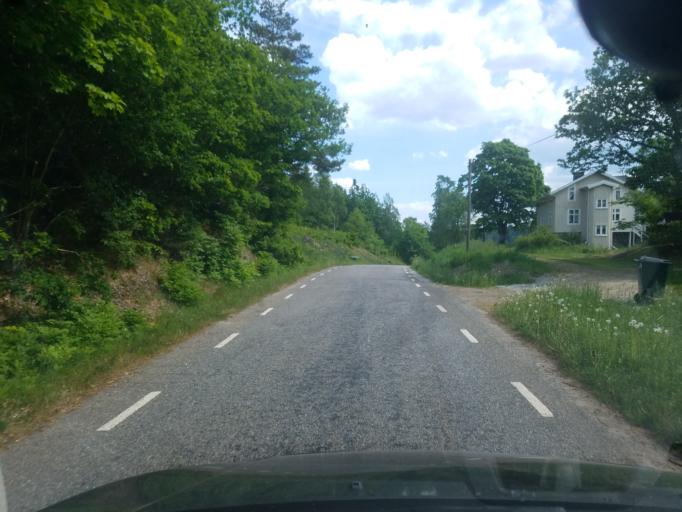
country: SE
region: Vaestra Goetaland
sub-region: Stenungsunds Kommun
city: Stora Hoga
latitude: 58.0007
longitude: 11.9300
